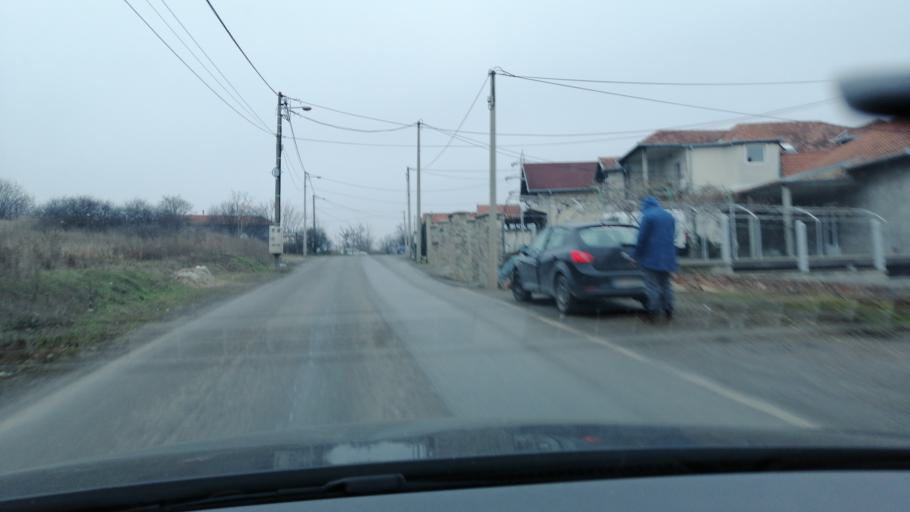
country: RS
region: Central Serbia
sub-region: Belgrade
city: Zvezdara
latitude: 44.7786
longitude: 20.5474
